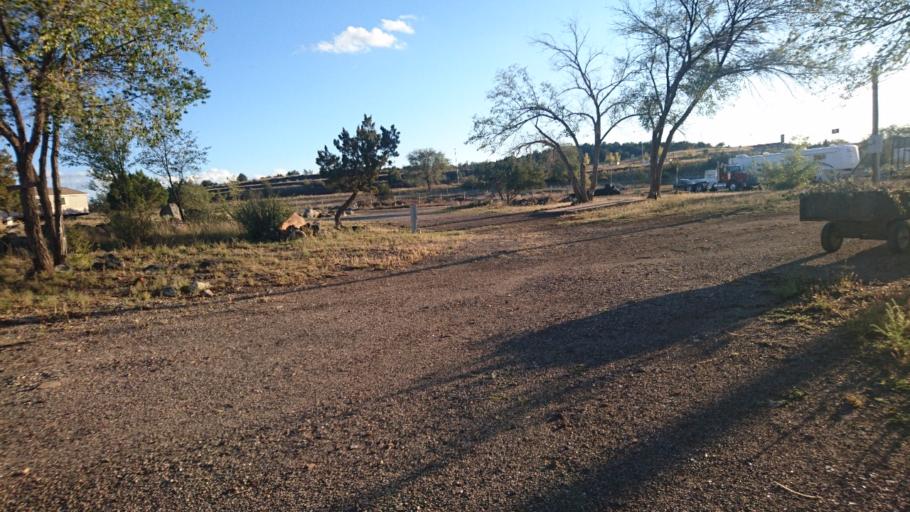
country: US
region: Arizona
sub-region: Coconino County
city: Williams
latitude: 35.2213
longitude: -112.4923
